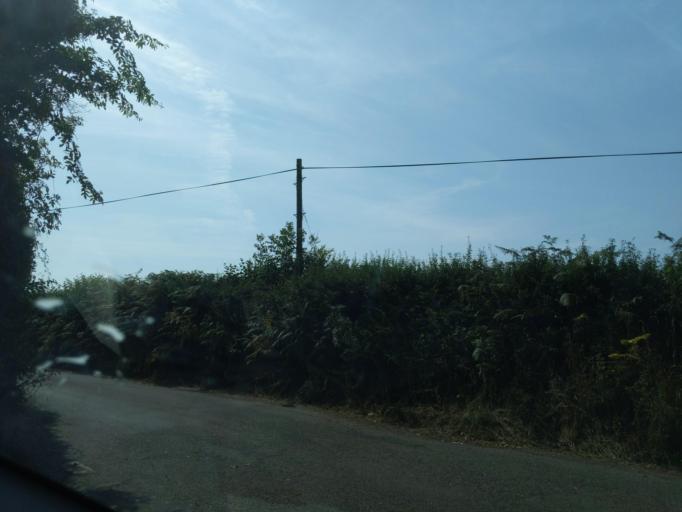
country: GB
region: England
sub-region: Devon
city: Winkleigh
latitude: 50.8750
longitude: -3.8715
